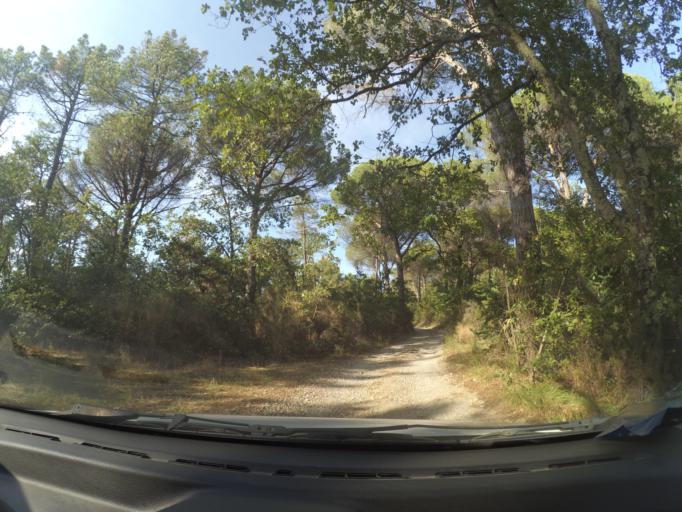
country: IT
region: Tuscany
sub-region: Province of Arezzo
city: Castiglion Fibocchi
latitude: 43.5315
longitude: 11.7825
